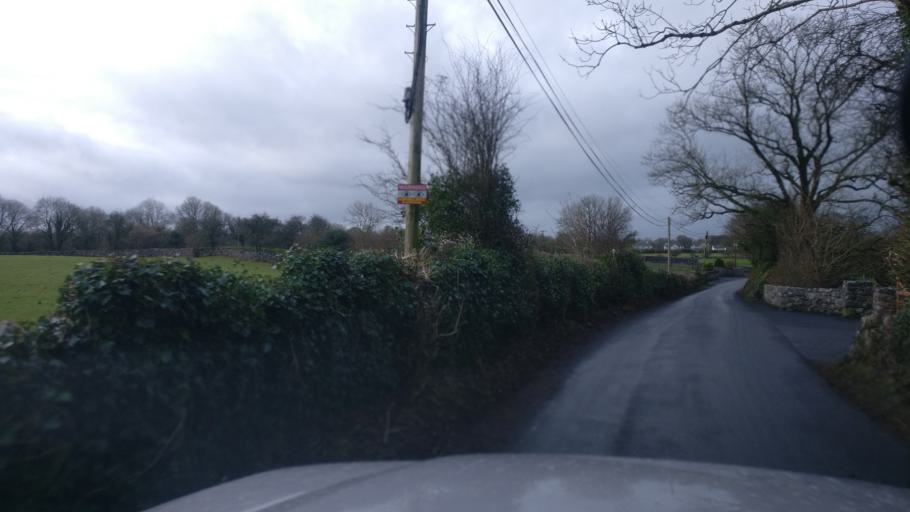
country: IE
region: Connaught
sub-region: County Galway
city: Athenry
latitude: 53.2672
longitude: -8.7785
